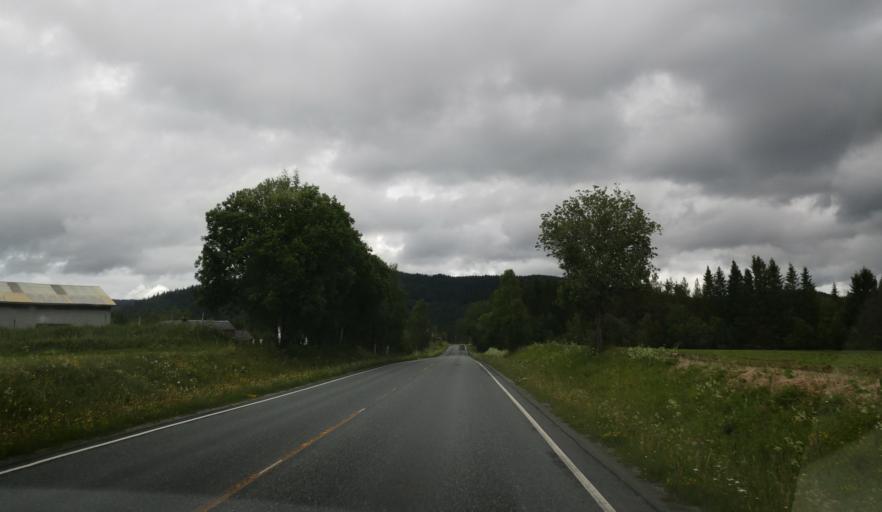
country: NO
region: Sor-Trondelag
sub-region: Selbu
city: Mebonden
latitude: 63.3758
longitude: 11.0783
